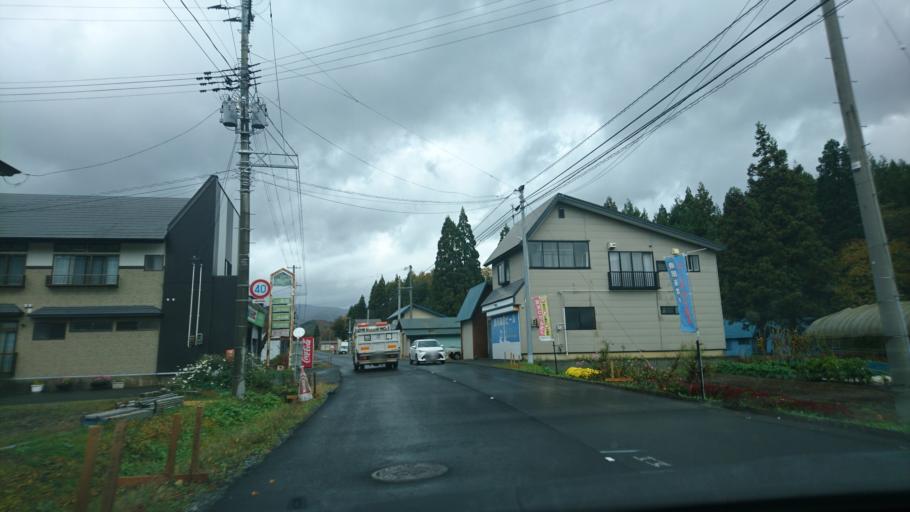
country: JP
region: Iwate
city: Shizukuishi
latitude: 39.5177
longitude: 140.8294
